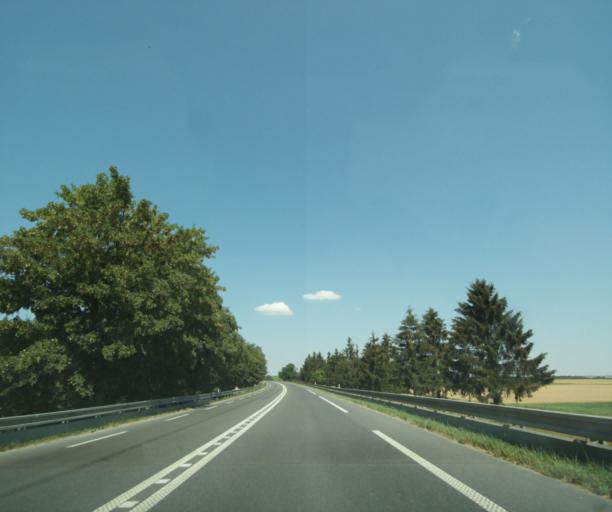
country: FR
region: Champagne-Ardenne
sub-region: Departement de la Marne
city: Verzy
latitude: 49.1374
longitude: 4.2298
